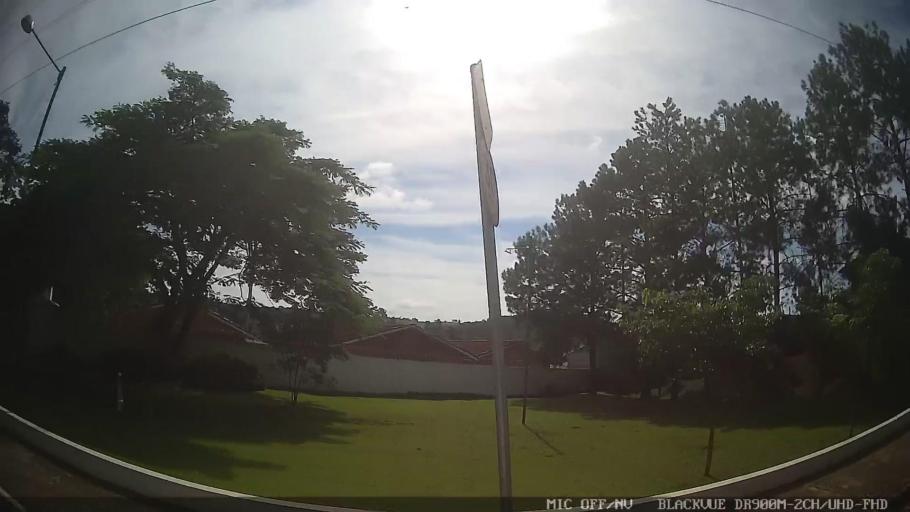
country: BR
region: Sao Paulo
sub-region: Jarinu
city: Jarinu
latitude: -23.0574
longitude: -46.6416
